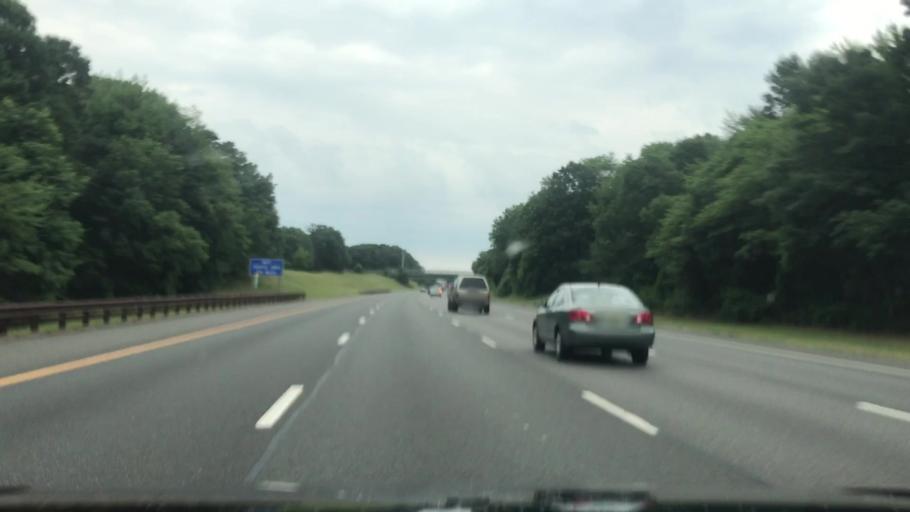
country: US
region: New Jersey
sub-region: Monmouth County
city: Shark River Hills
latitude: 40.2073
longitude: -74.0984
